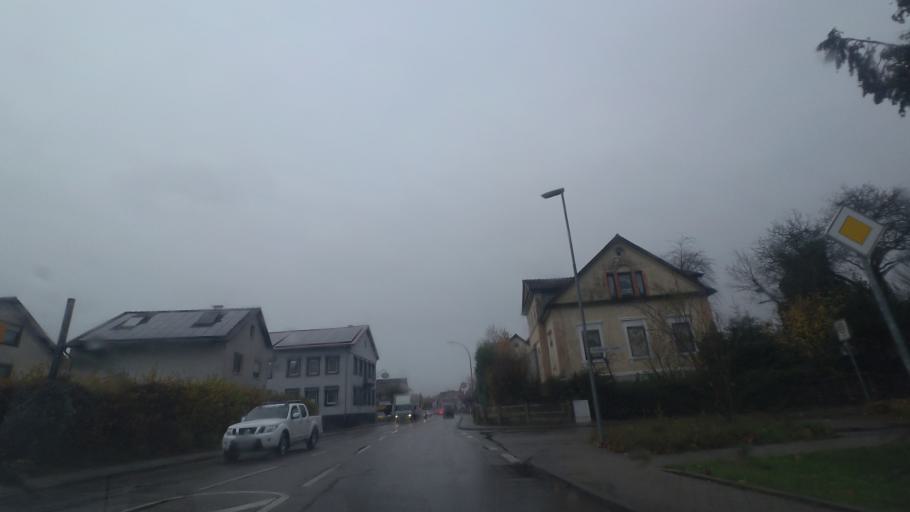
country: DE
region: Baden-Wuerttemberg
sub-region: Karlsruhe Region
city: Sinzheim
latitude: 48.7586
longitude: 8.1683
